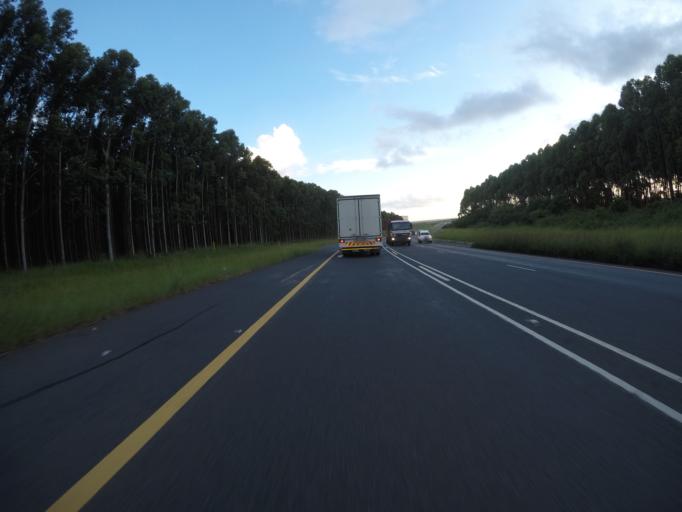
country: ZA
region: KwaZulu-Natal
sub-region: uThungulu District Municipality
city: KwaMbonambi
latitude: -28.5925
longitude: 32.0999
